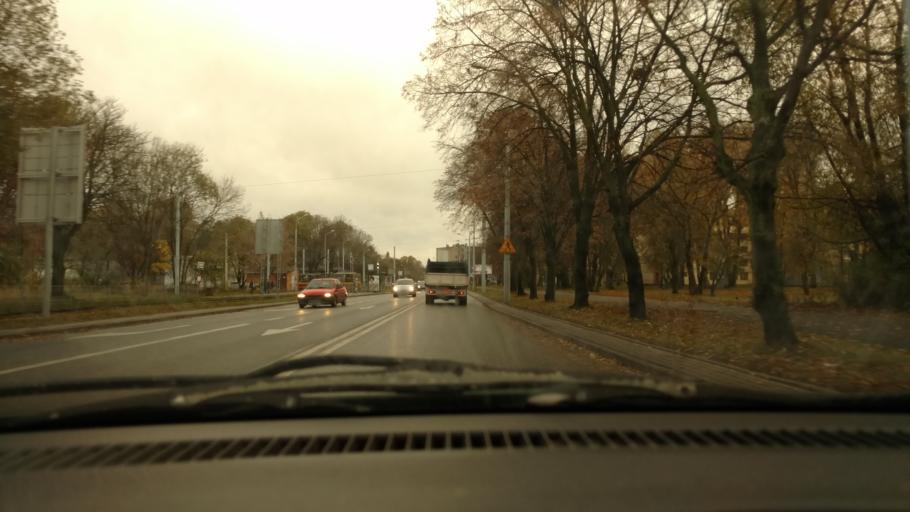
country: PL
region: Lodz Voivodeship
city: Lodz
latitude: 51.7774
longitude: 19.4984
